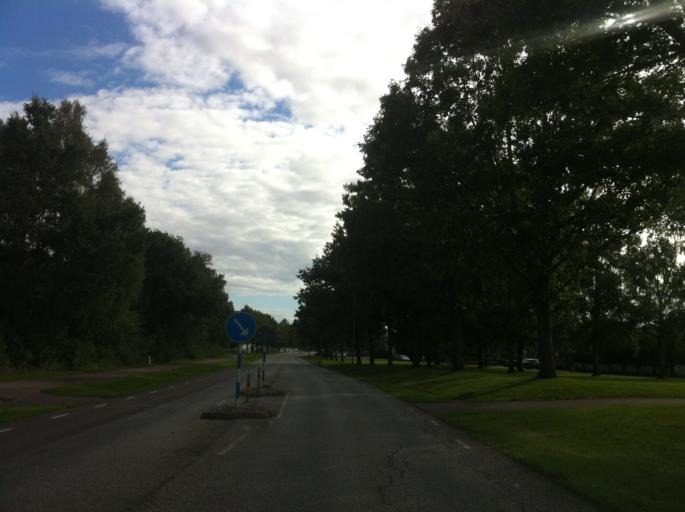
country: SE
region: Skane
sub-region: Bastads Kommun
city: Bastad
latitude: 56.3891
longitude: 12.9220
